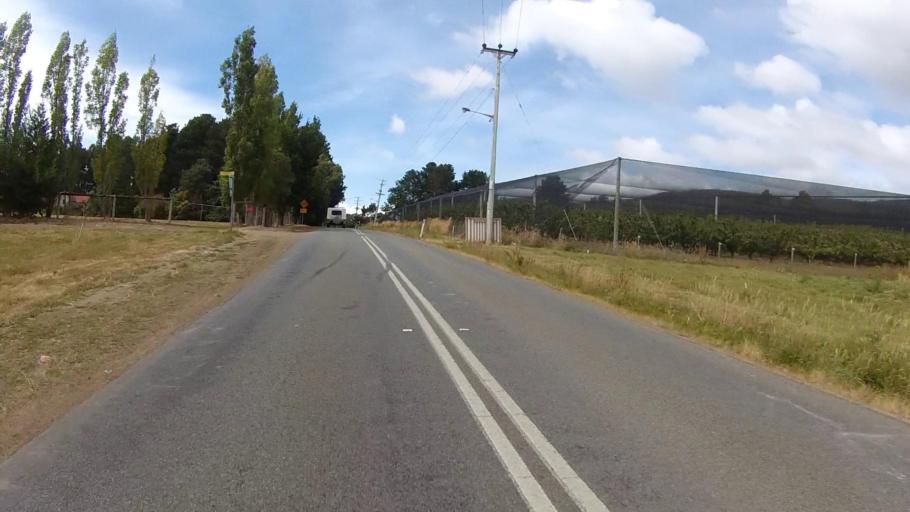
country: AU
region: Tasmania
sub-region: Kingborough
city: Kettering
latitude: -43.1756
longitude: 147.2362
